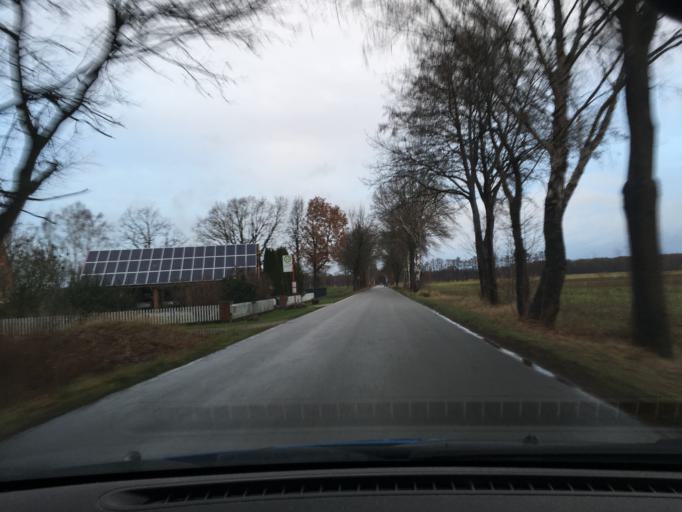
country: DE
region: Lower Saxony
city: Hittbergen
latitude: 53.3106
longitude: 10.6163
